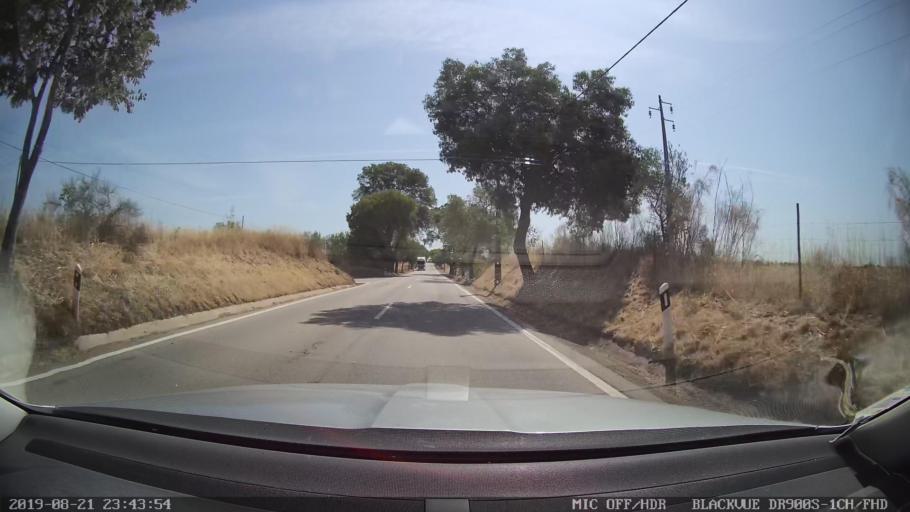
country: PT
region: Castelo Branco
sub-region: Idanha-A-Nova
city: Idanha-a-Nova
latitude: 39.8483
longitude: -7.2878
